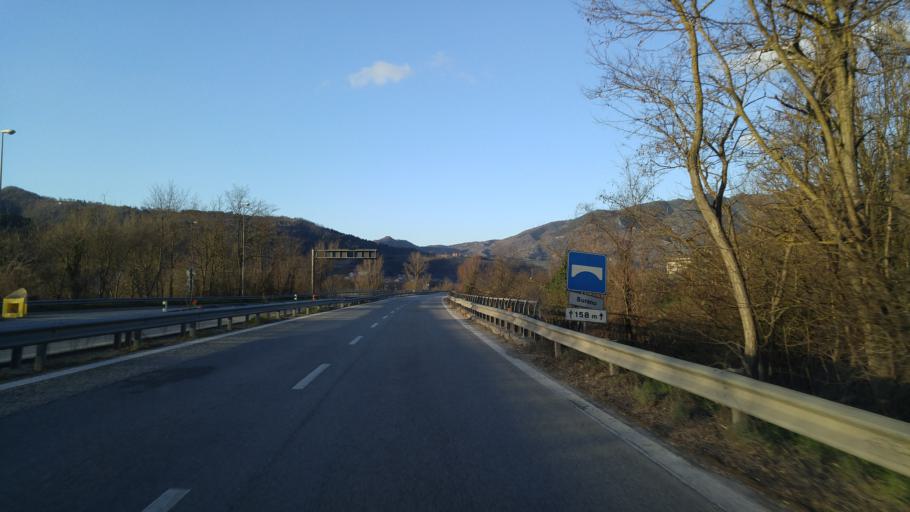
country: IT
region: The Marches
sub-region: Provincia di Pesaro e Urbino
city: Acqualagna
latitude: 43.6147
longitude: 12.6754
